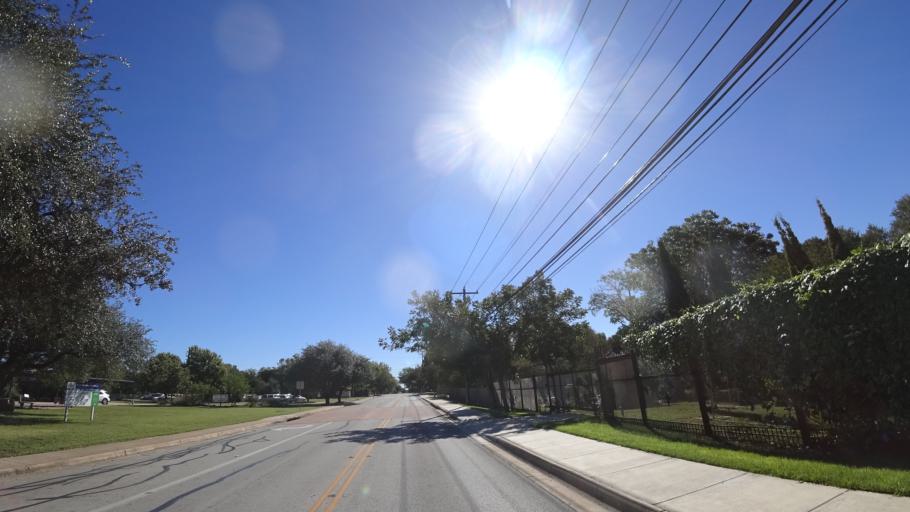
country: US
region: Texas
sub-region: Travis County
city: Rollingwood
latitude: 30.2273
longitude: -97.8074
